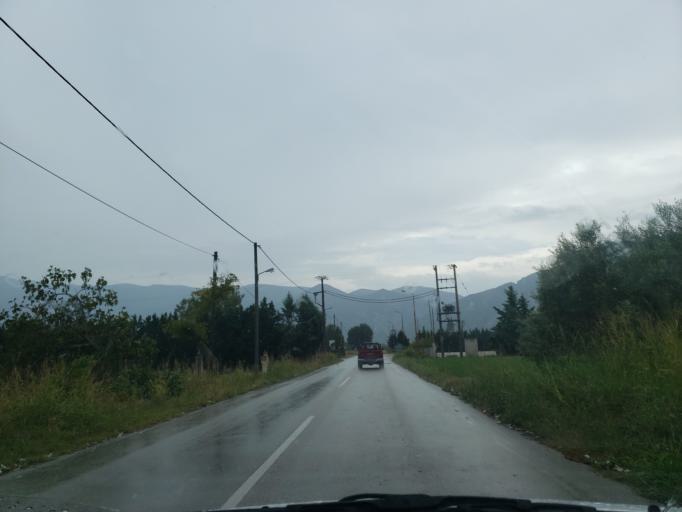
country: GR
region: Central Greece
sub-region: Nomos Fthiotidos
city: Anthili
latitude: 38.8212
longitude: 22.4419
